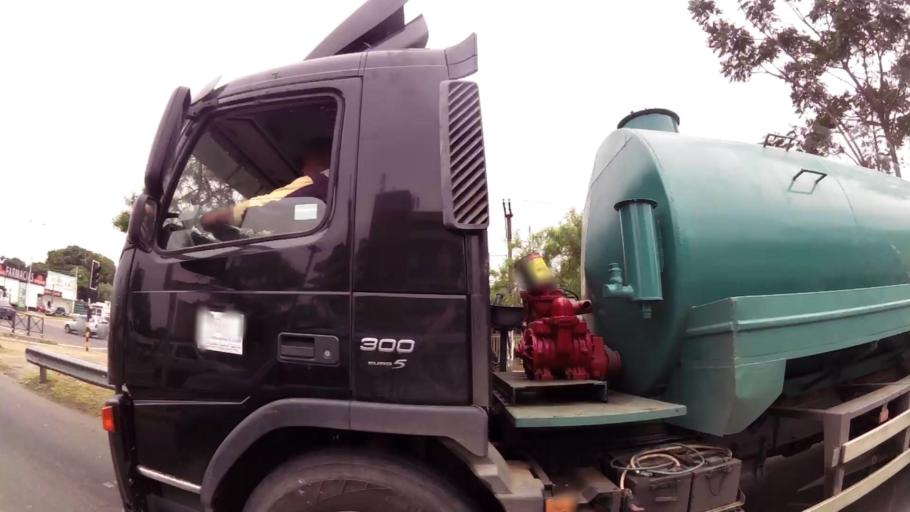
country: BO
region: Santa Cruz
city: Santa Cruz de la Sierra
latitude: -17.7790
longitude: -63.1936
